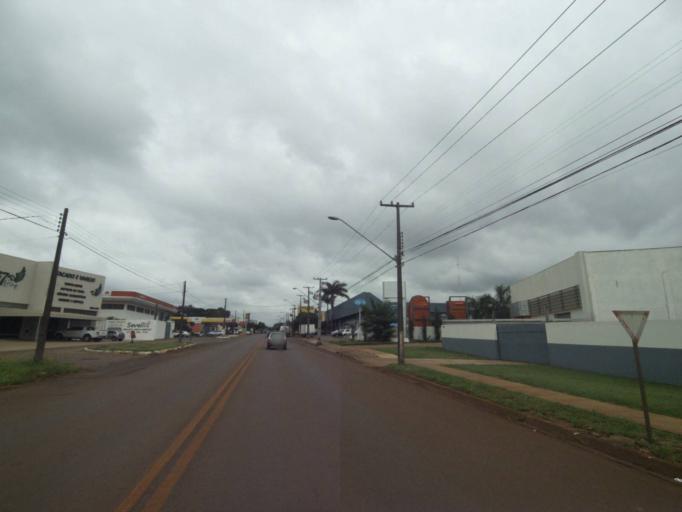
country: BR
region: Parana
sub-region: Campo Mourao
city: Campo Mourao
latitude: -24.0282
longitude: -52.3654
